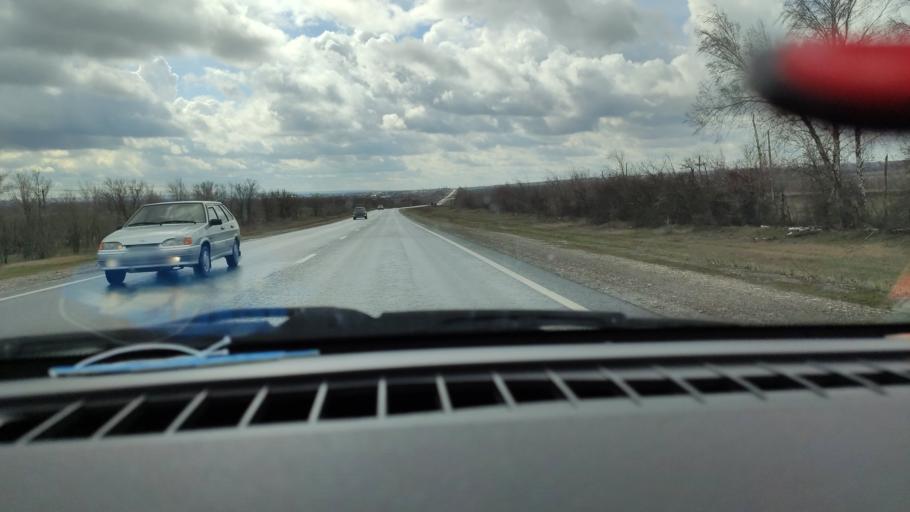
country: RU
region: Samara
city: Yelkhovka
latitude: 53.9023
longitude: 50.2682
